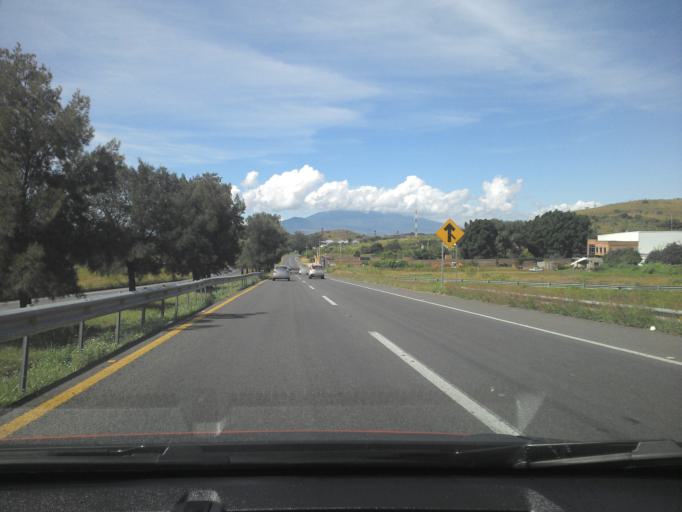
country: MX
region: Jalisco
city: La Venta del Astillero
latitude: 20.7364
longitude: -103.5815
